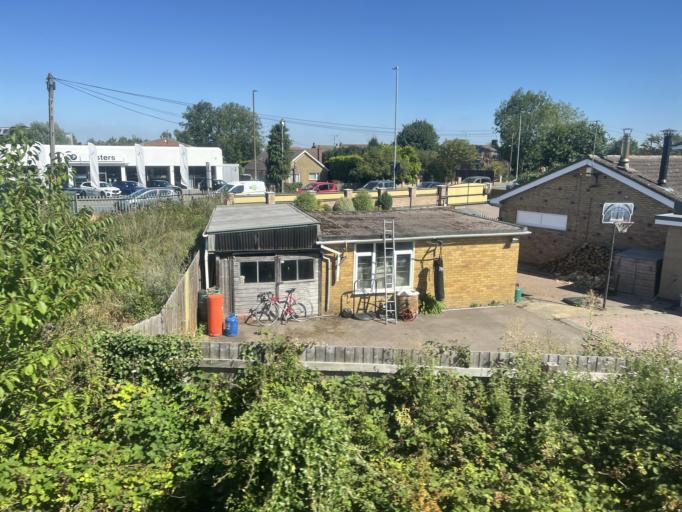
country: GB
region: England
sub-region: Lincolnshire
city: Boston
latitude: 52.9722
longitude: -0.0581
